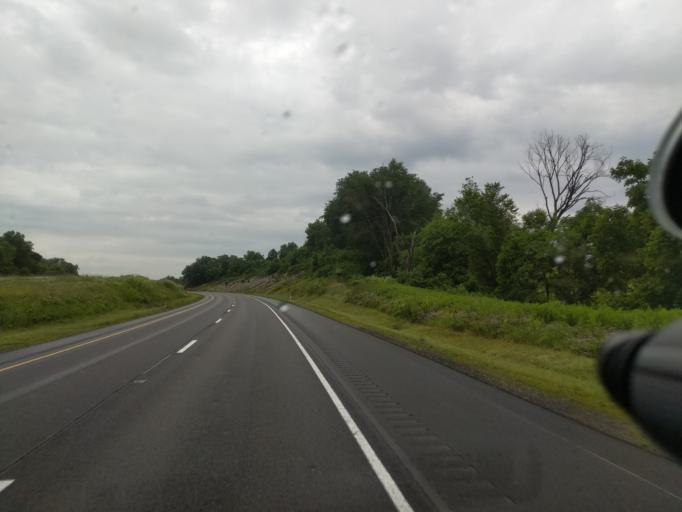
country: US
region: Pennsylvania
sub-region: Northumberland County
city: Milton
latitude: 41.0413
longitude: -76.8123
